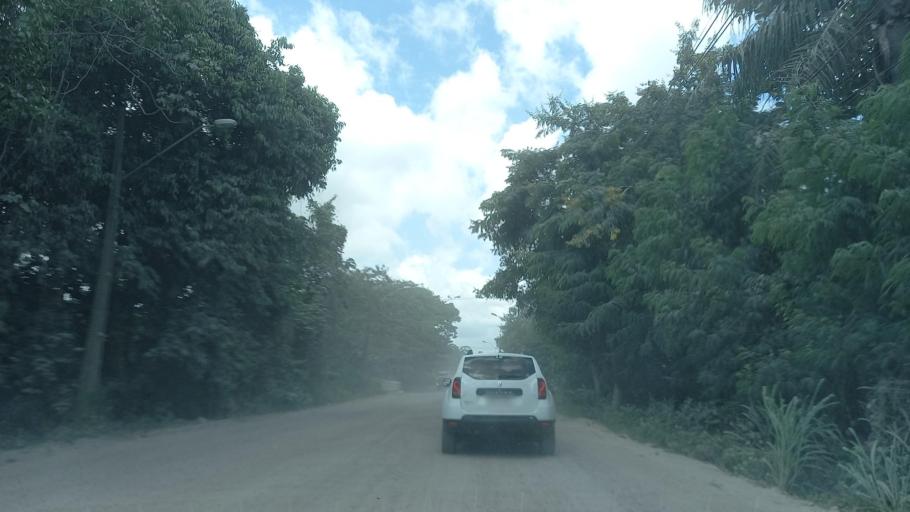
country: BR
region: Pernambuco
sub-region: Jaboatao Dos Guararapes
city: Jaboatao
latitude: -8.1593
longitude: -34.9795
